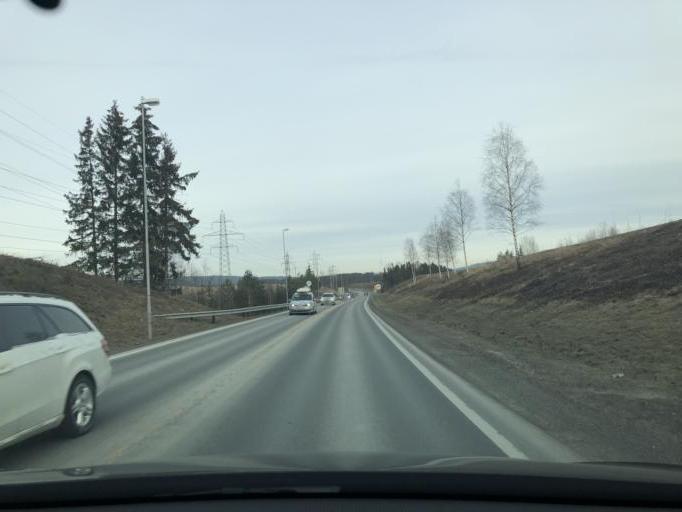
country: NO
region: Buskerud
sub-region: Ringerike
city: Honefoss
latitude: 60.1758
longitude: 10.2215
